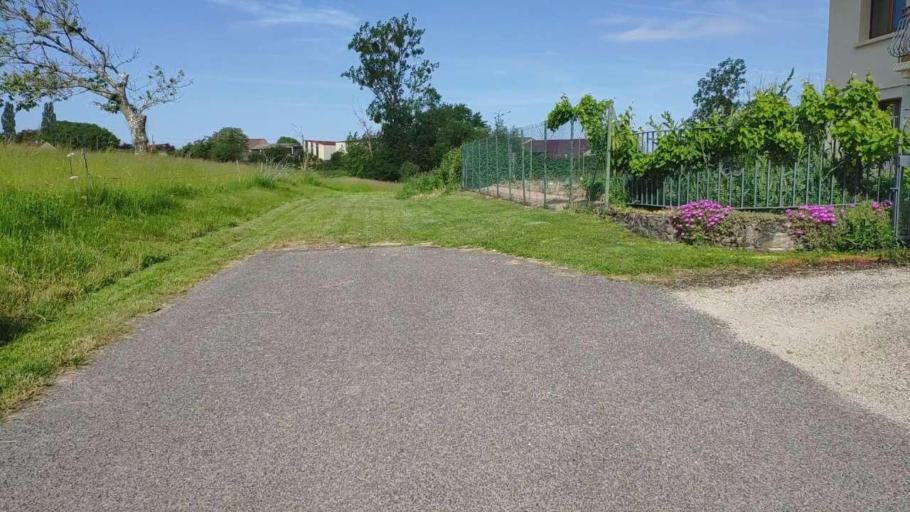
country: FR
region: Franche-Comte
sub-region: Departement du Jura
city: Bletterans
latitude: 46.7137
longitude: 5.4697
